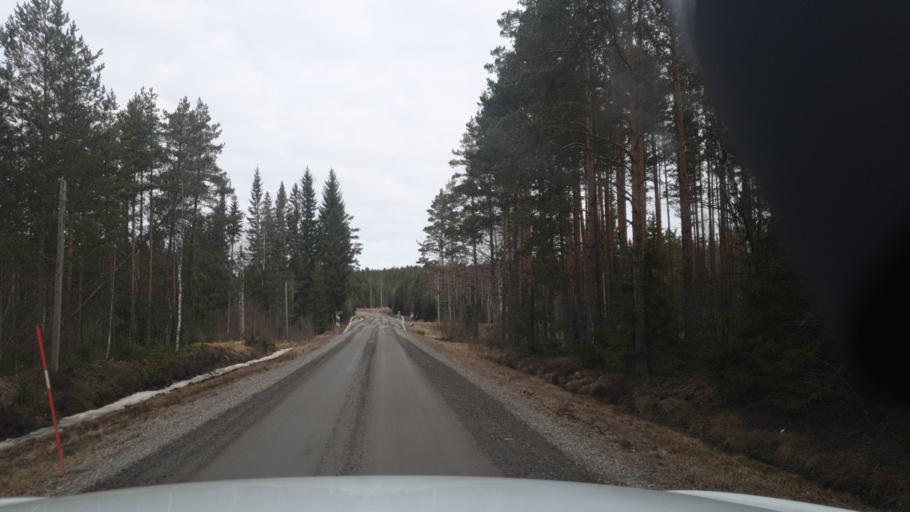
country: SE
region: Vaermland
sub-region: Eda Kommun
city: Charlottenberg
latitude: 59.9678
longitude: 12.5039
